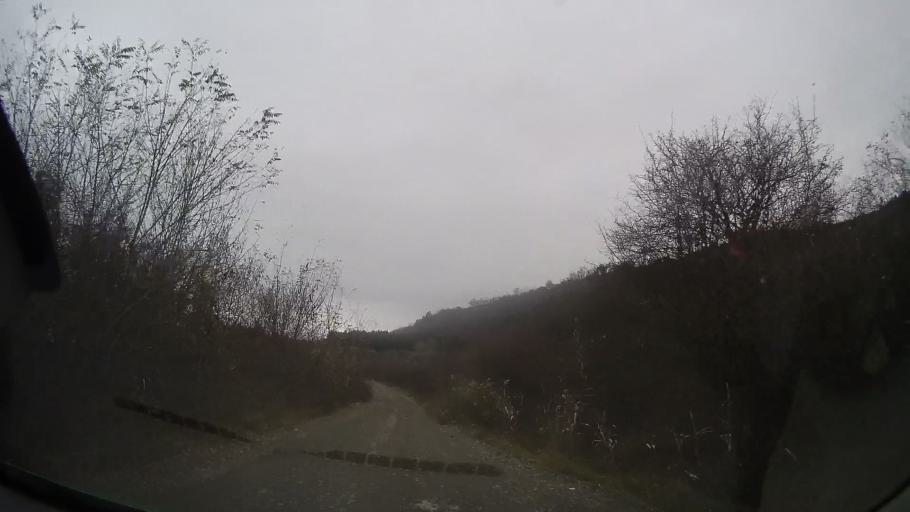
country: RO
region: Mures
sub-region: Comuna Bala
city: Bala
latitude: 46.6821
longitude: 24.4870
